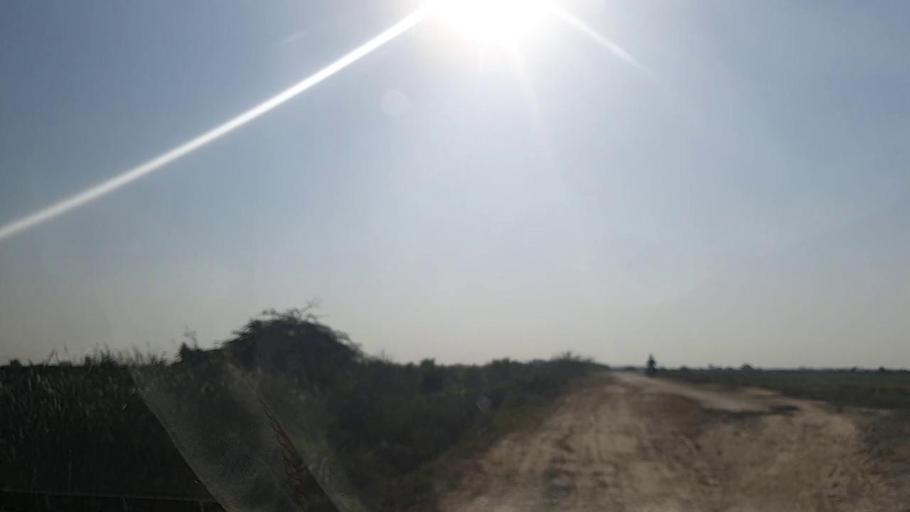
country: PK
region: Sindh
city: Mirpur Batoro
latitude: 24.5540
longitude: 68.1696
